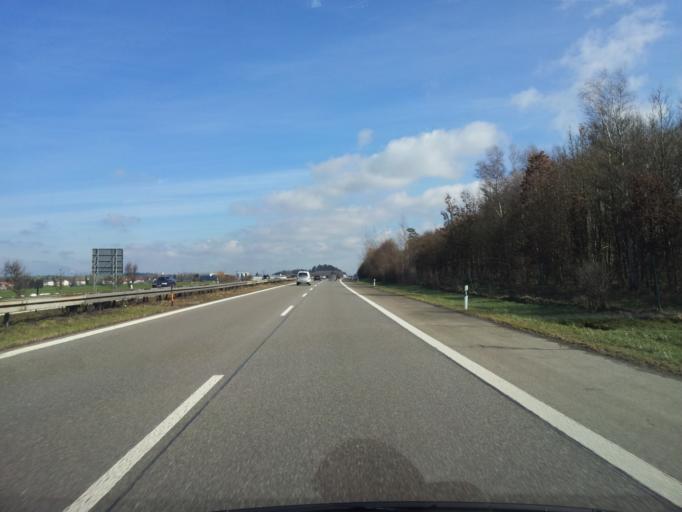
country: DE
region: Baden-Wuerttemberg
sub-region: Freiburg Region
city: Tuningen
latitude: 48.0193
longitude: 8.6096
